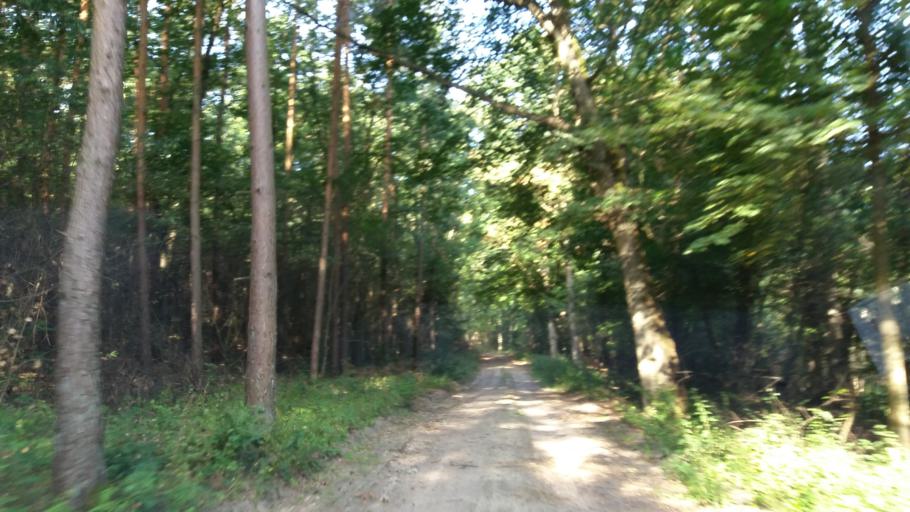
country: PL
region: West Pomeranian Voivodeship
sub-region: Powiat choszczenski
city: Choszczno
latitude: 53.2357
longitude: 15.4399
